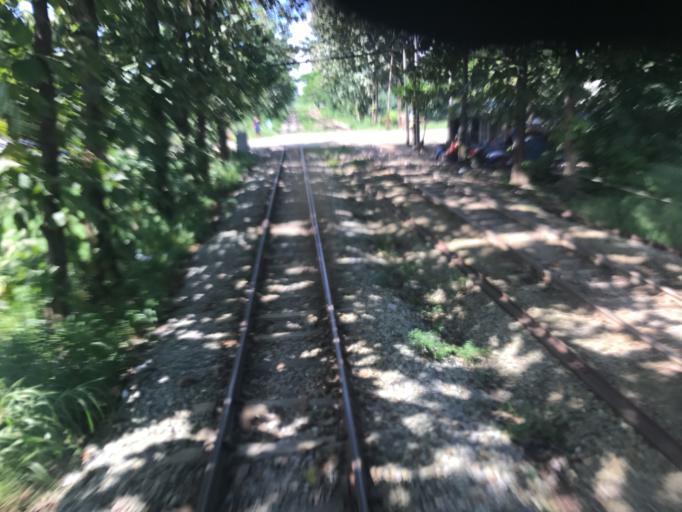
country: MM
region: Yangon
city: Yangon
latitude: 16.9573
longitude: 96.0883
